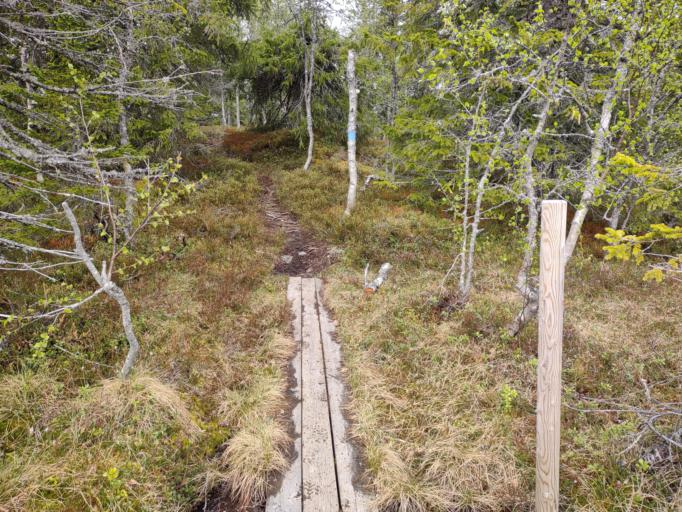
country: NO
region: Oppland
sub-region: Gran
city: Jaren
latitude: 60.4291
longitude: 10.6690
